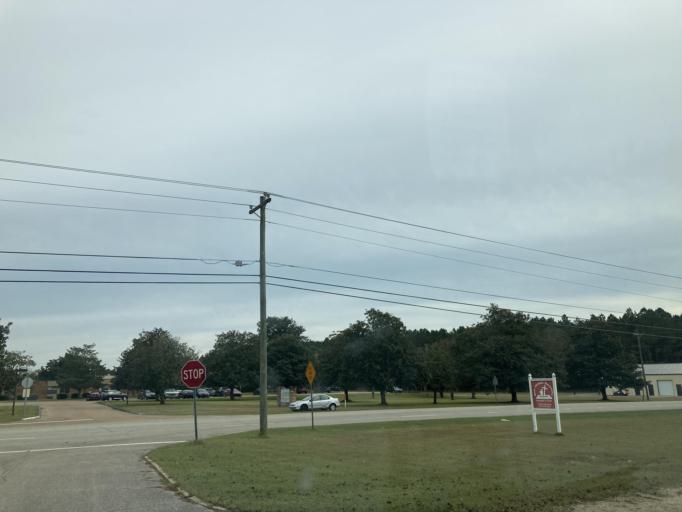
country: US
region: Mississippi
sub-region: Lamar County
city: Purvis
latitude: 31.0994
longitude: -89.4139
